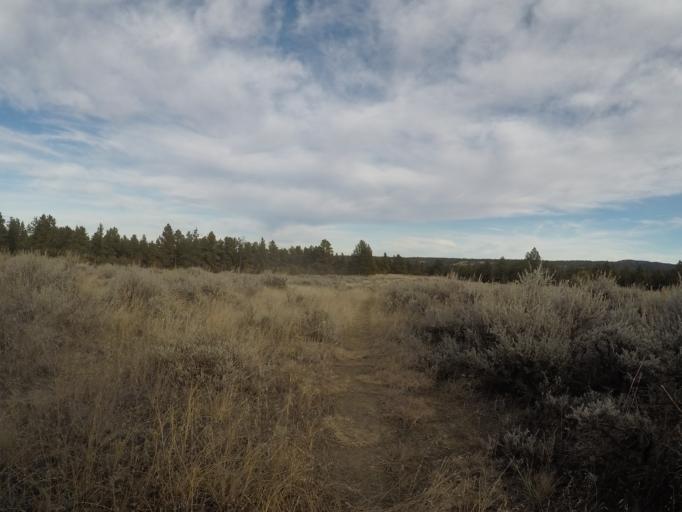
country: US
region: Montana
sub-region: Musselshell County
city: Roundup
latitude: 46.2736
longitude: -108.7452
